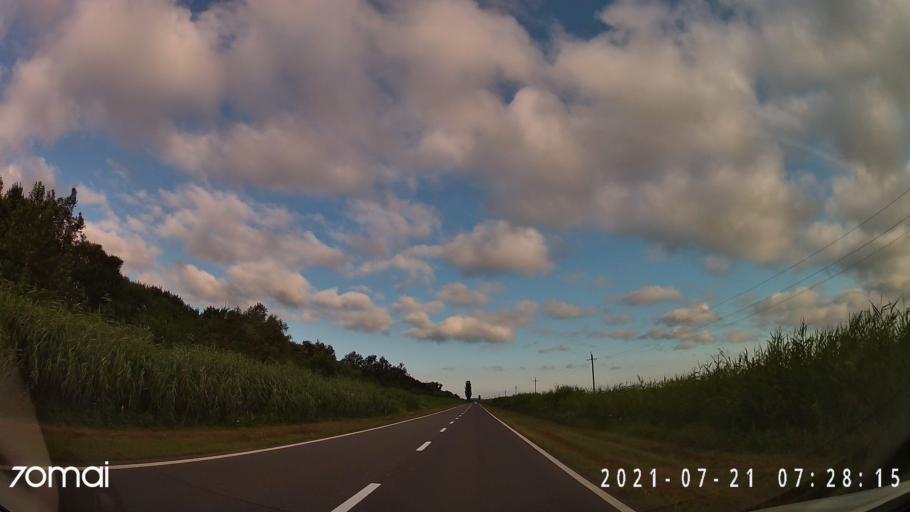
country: RO
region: Tulcea
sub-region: Comuna Luncavita
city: Rachelu
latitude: 45.3094
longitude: 28.3974
